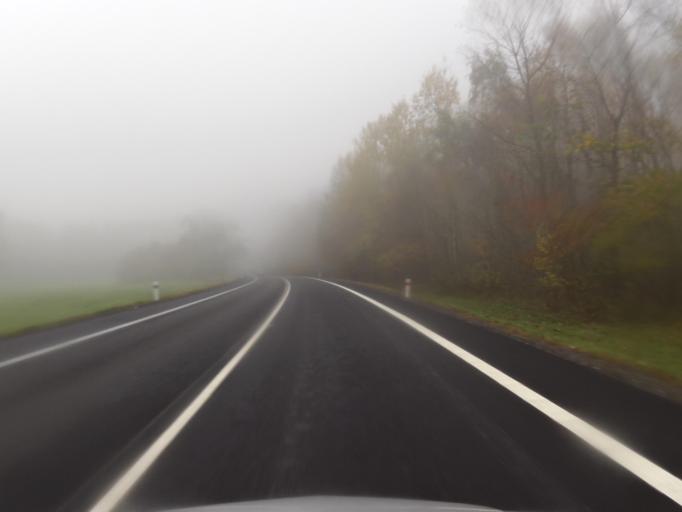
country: CZ
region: Ustecky
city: Libouchec
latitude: 50.7219
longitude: 13.9960
